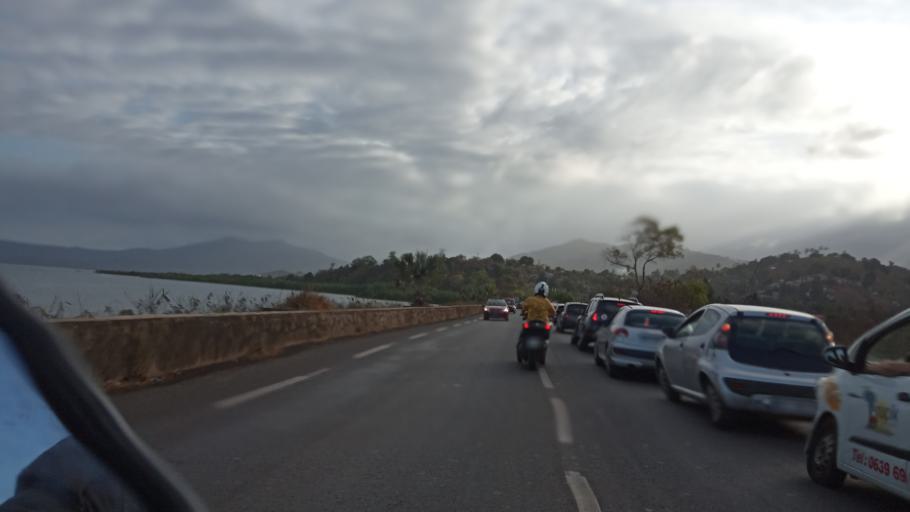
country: YT
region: Mamoudzou
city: Mamoudzou
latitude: -12.7930
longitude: 45.2200
